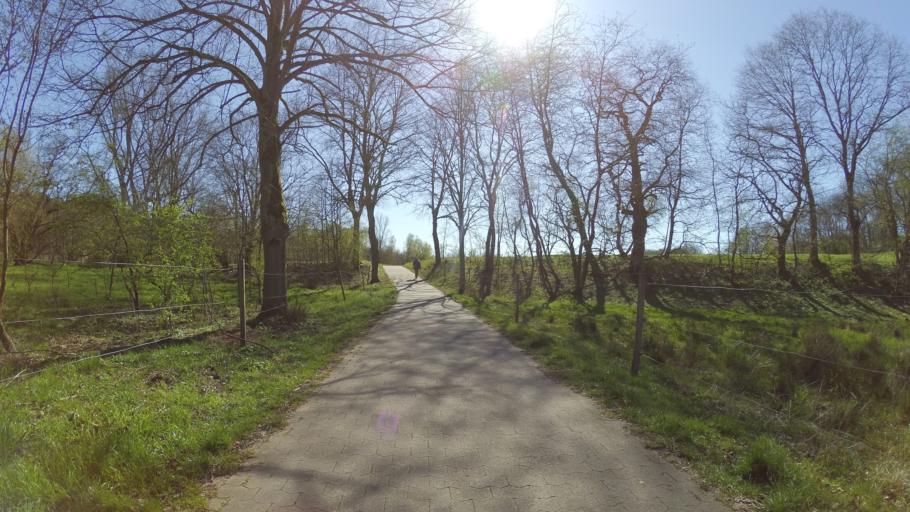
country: DE
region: Saarland
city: Puttlingen
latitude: 49.2986
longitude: 6.8942
